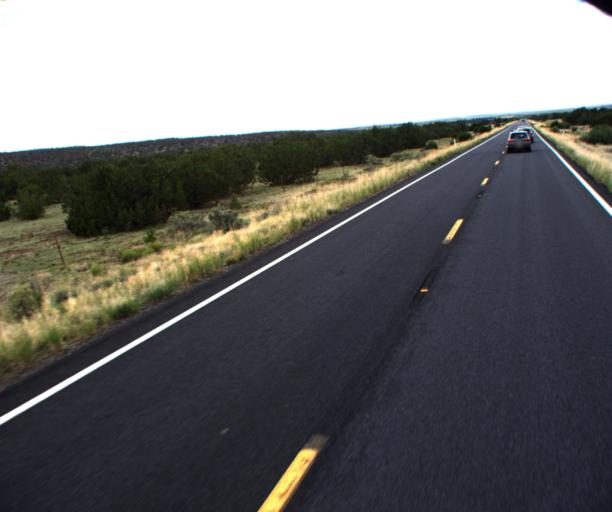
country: US
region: Arizona
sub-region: Coconino County
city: Parks
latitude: 35.5797
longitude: -111.9497
